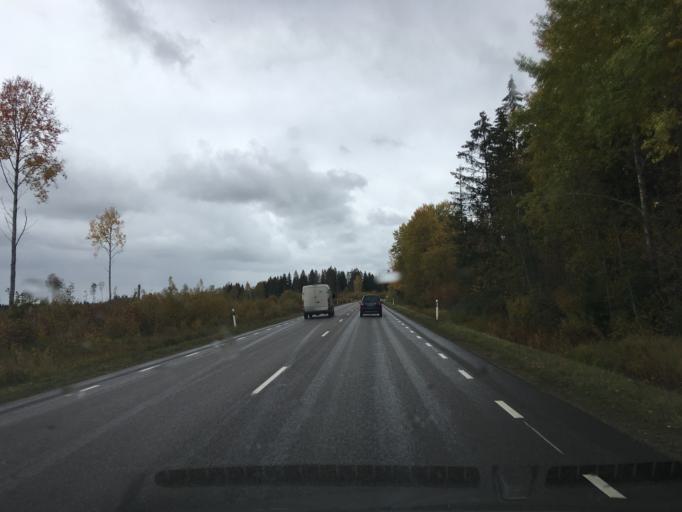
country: EE
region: Harju
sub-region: Anija vald
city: Kehra
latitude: 59.3372
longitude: 25.3110
